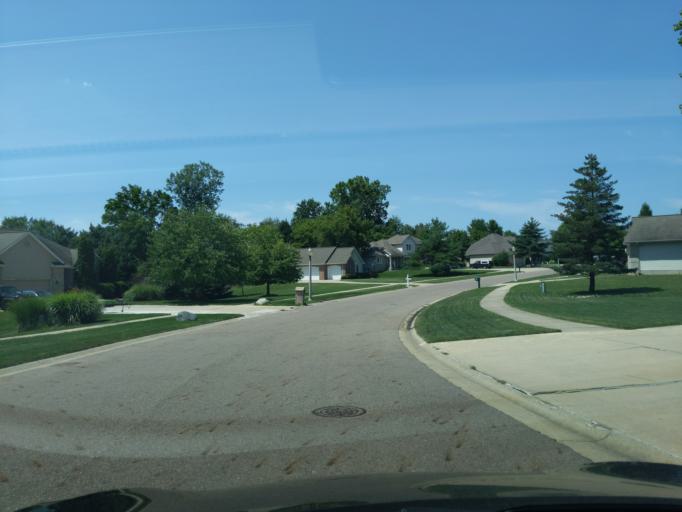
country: US
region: Michigan
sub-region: Ingham County
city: Edgemont Park
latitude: 42.7639
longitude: -84.6084
